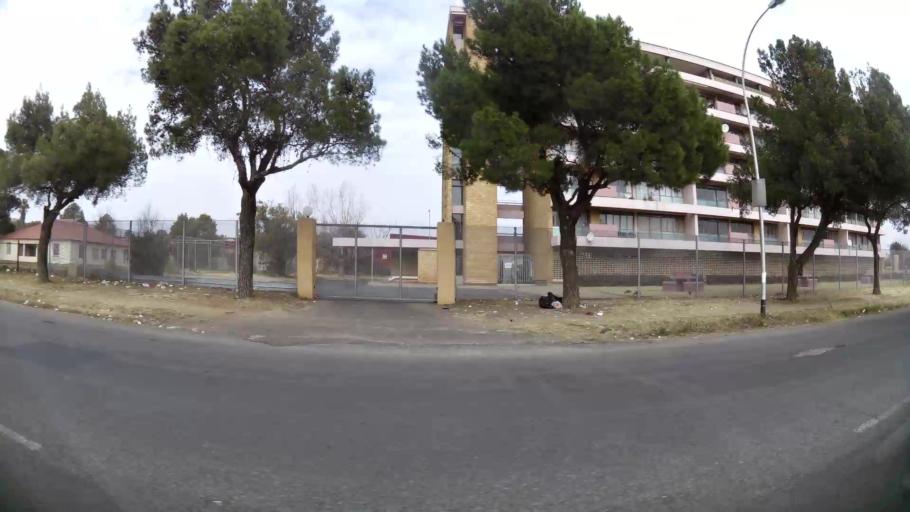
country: ZA
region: Orange Free State
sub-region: Mangaung Metropolitan Municipality
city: Bloemfontein
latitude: -29.1261
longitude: 26.2038
